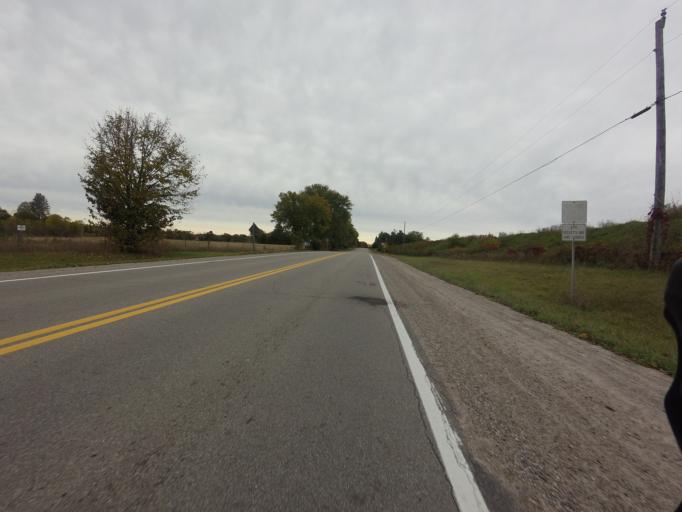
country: CA
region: Ontario
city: Gananoque
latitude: 44.4951
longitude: -76.1870
